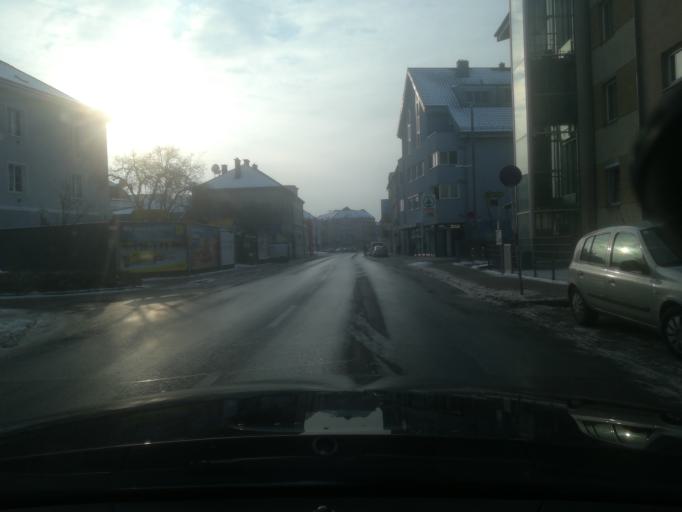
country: AT
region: Upper Austria
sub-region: Wels Stadt
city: Wels
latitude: 48.1699
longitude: 14.0243
